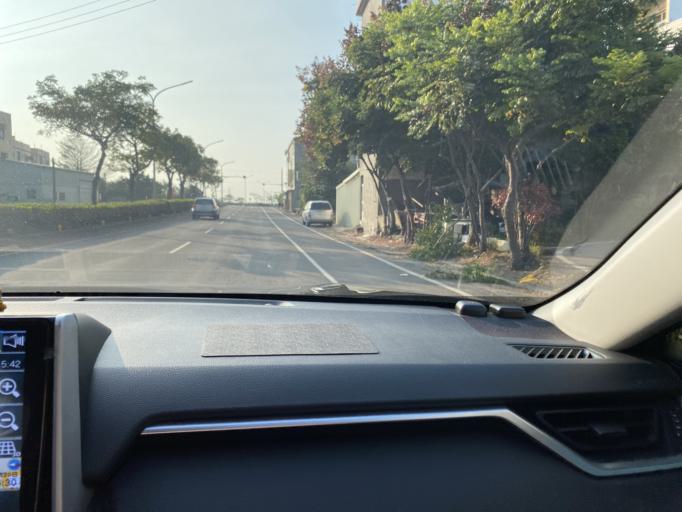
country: TW
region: Taiwan
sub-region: Changhua
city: Chang-hua
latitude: 23.9534
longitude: 120.4198
